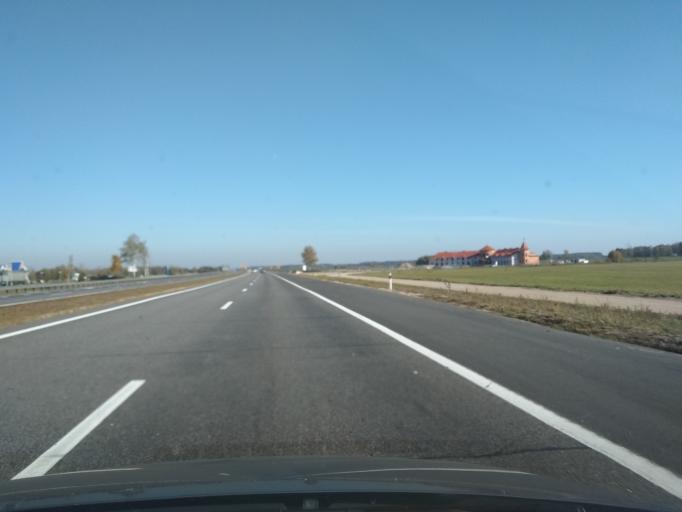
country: BY
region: Brest
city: Byaroza
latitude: 52.4950
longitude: 24.9809
